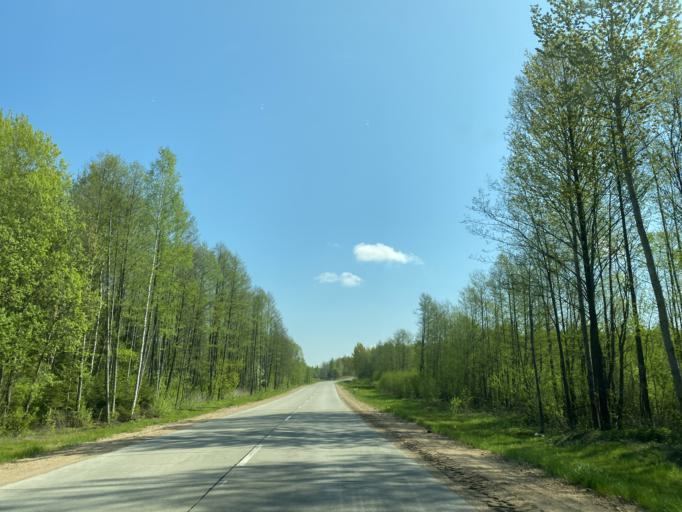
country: BY
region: Minsk
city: Horad Barysaw
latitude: 54.1759
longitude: 28.5334
